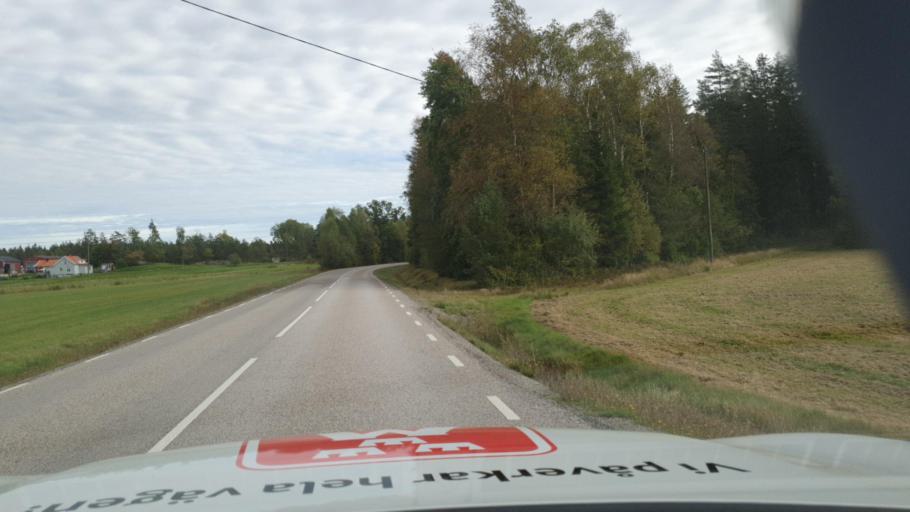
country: SE
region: Vaestra Goetaland
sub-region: Fargelanda Kommun
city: Faergelanda
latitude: 58.4320
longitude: 12.1038
